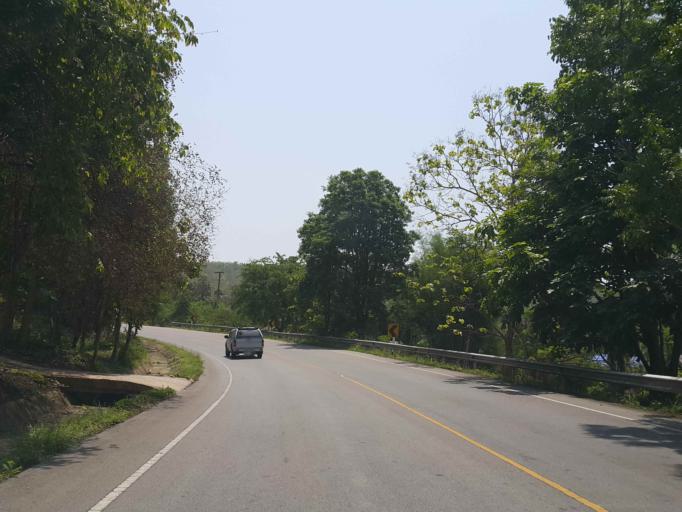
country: TH
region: Chiang Mai
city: Mae Taeng
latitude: 19.0888
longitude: 98.9977
